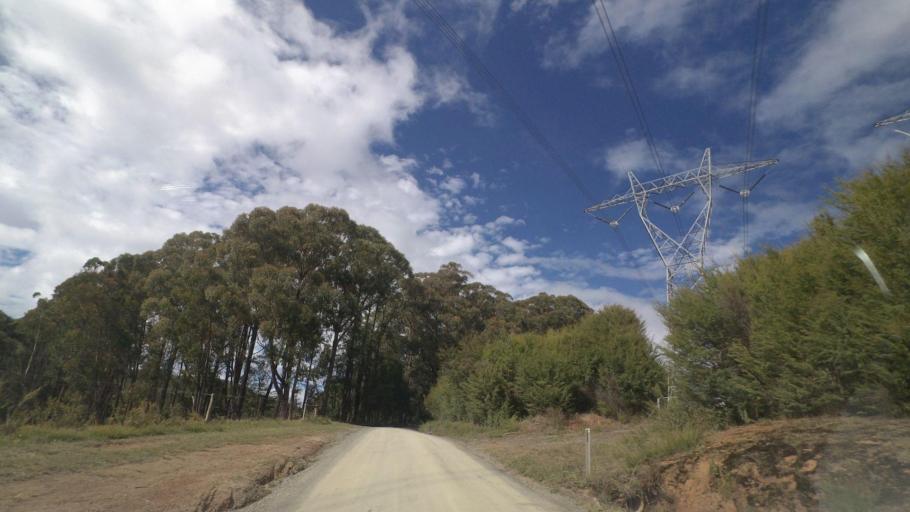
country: AU
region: Victoria
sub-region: Cardinia
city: Gembrook
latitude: -37.8842
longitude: 145.6091
